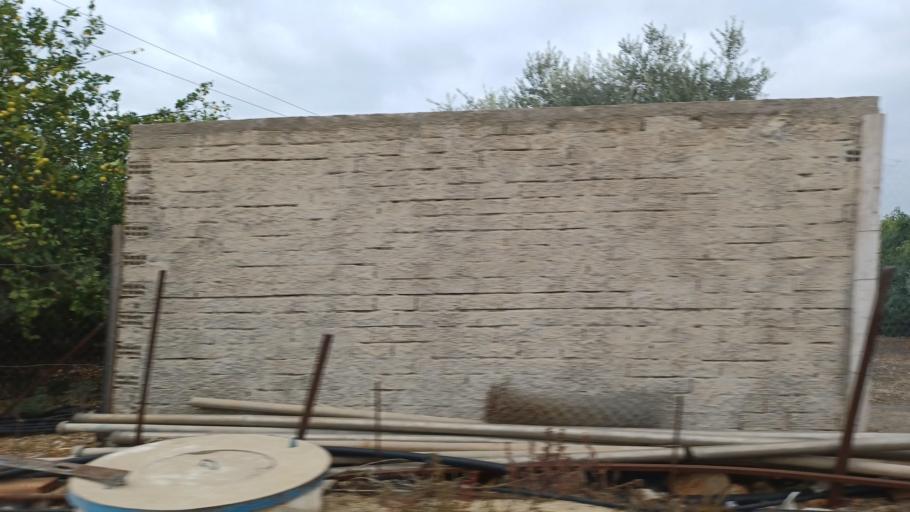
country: CY
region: Pafos
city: Pegeia
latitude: 34.8951
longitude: 32.3358
